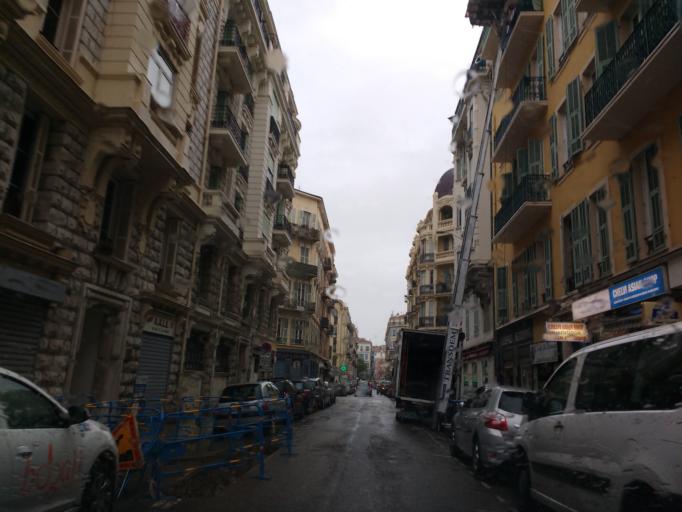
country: FR
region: Provence-Alpes-Cote d'Azur
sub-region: Departement des Alpes-Maritimes
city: Nice
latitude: 43.7058
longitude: 7.2681
